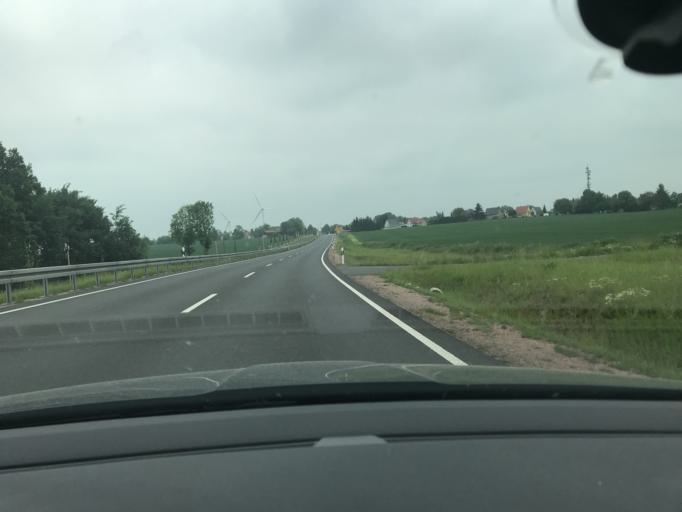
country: DE
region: Saxony
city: Nossen
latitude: 51.0994
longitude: 13.3590
